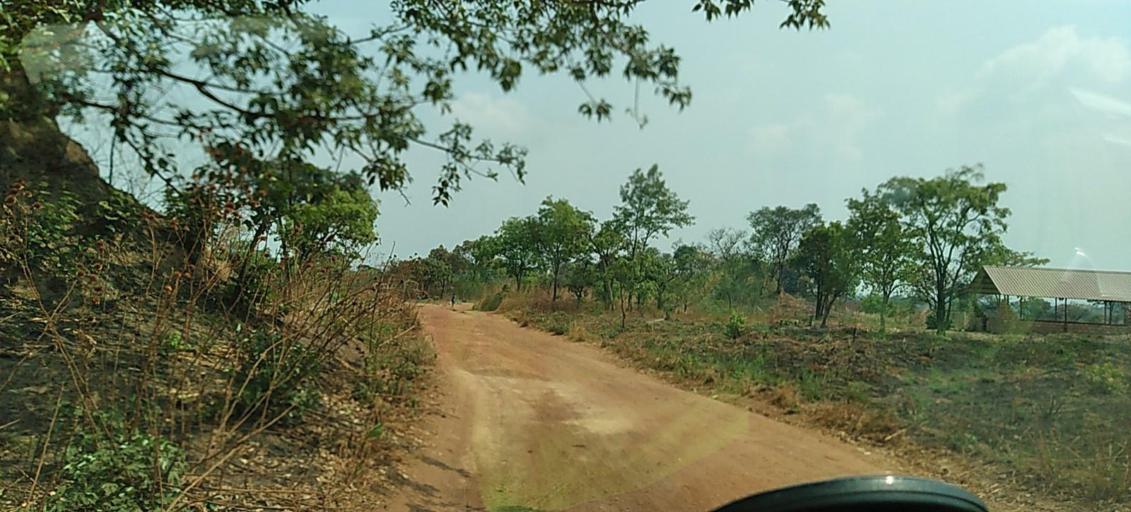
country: ZM
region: North-Western
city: Kansanshi
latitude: -12.0912
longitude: 26.3654
